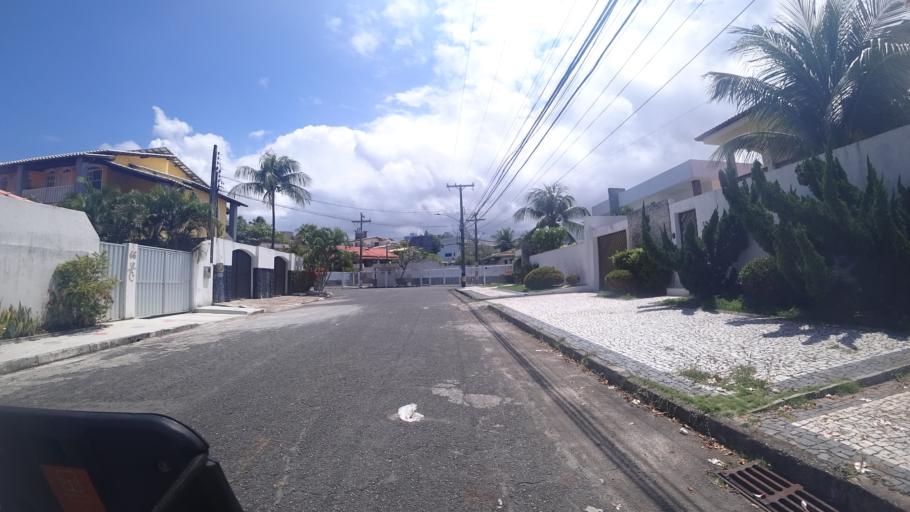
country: BR
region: Bahia
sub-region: Salvador
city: Salvador
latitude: -12.9940
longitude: -38.4673
